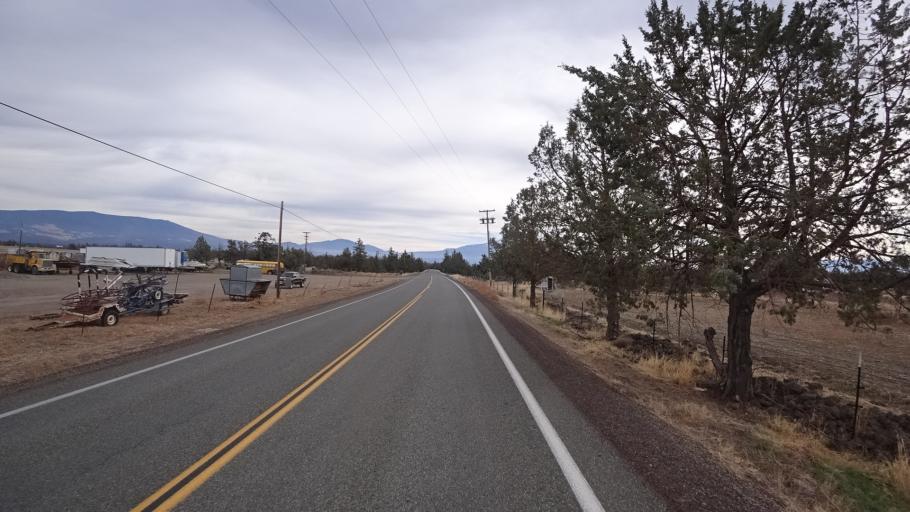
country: US
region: California
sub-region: Siskiyou County
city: Montague
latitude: 41.6281
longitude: -122.4313
